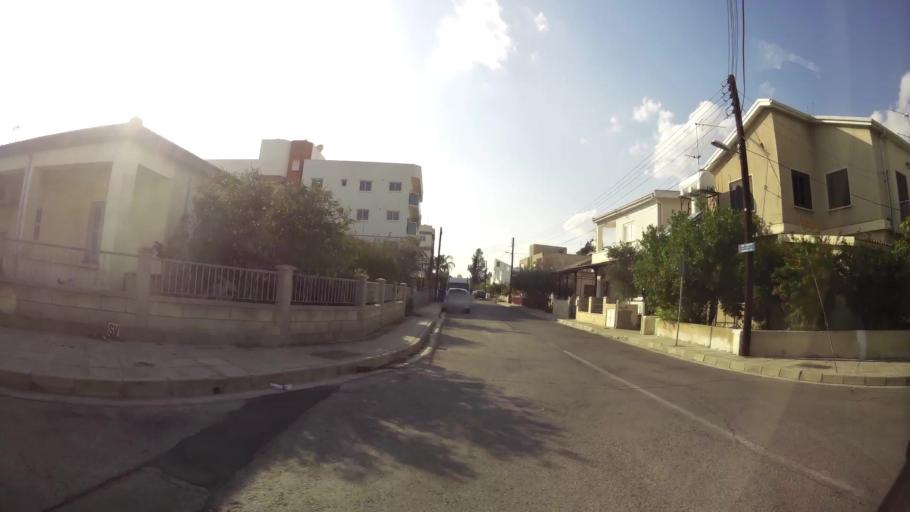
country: CY
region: Lefkosia
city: Nicosia
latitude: 35.1786
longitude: 33.3332
